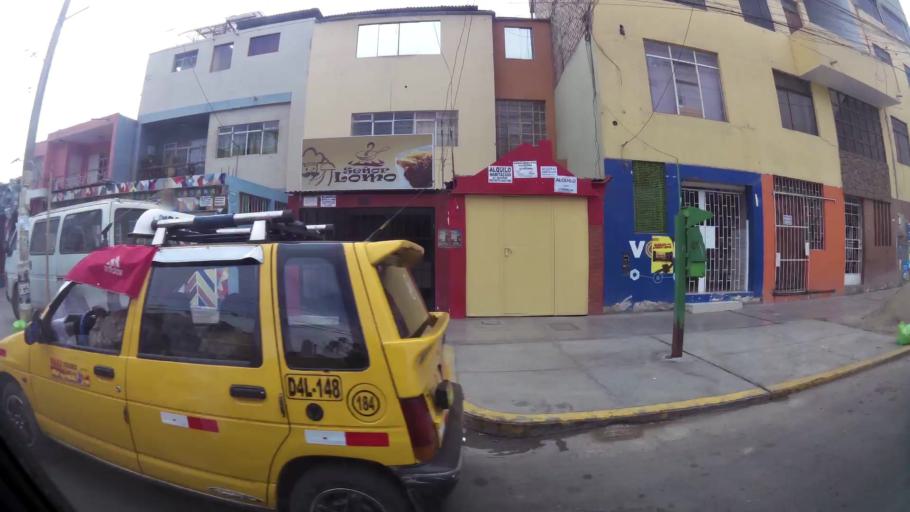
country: PE
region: La Libertad
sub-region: Provincia de Trujillo
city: Trujillo
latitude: -8.0985
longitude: -79.0186
